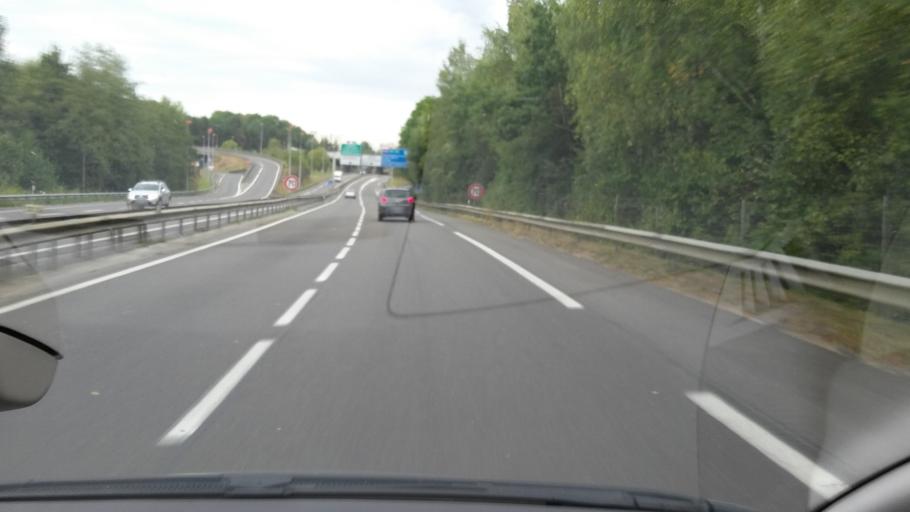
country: FR
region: Champagne-Ardenne
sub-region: Departement des Ardennes
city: La Francheville
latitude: 49.7313
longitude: 4.7201
